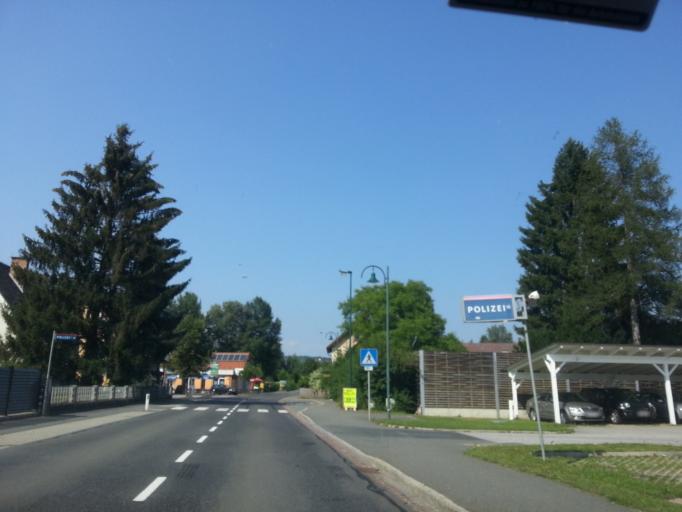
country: AT
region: Styria
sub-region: Politischer Bezirk Leibnitz
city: Heimschuh
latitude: 46.7589
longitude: 15.4880
